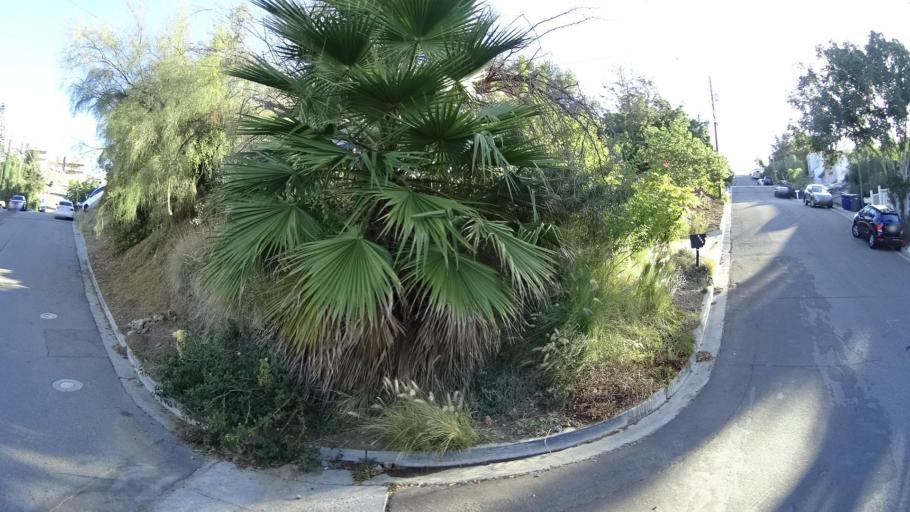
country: US
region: California
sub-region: San Diego County
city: La Presa
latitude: 32.7202
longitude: -116.9892
